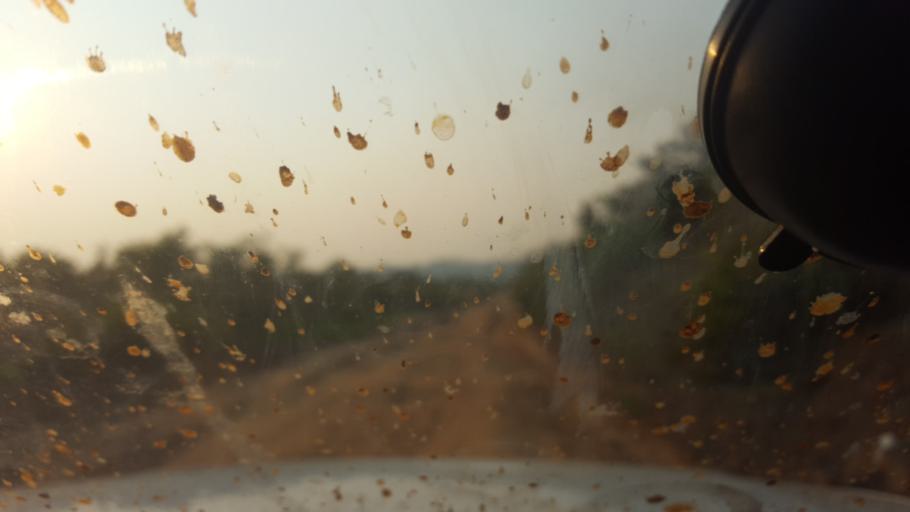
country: CD
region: Bandundu
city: Mushie
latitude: -3.7520
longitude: 16.6653
